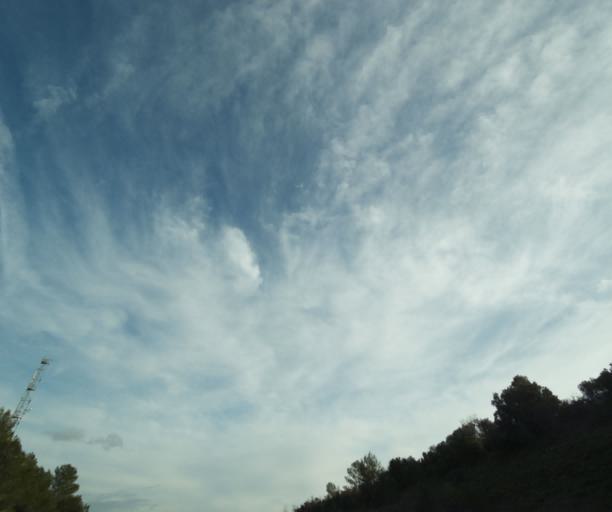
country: FR
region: Provence-Alpes-Cote d'Azur
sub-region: Departement du Var
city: Camps-la-Source
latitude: 43.4115
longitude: 6.1443
